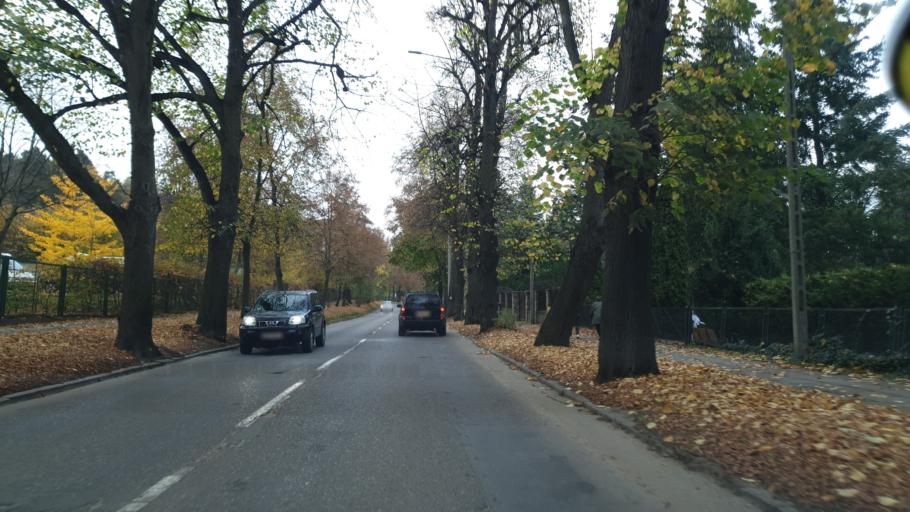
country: PL
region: Pomeranian Voivodeship
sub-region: Sopot
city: Sopot
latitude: 54.3954
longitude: 18.5659
